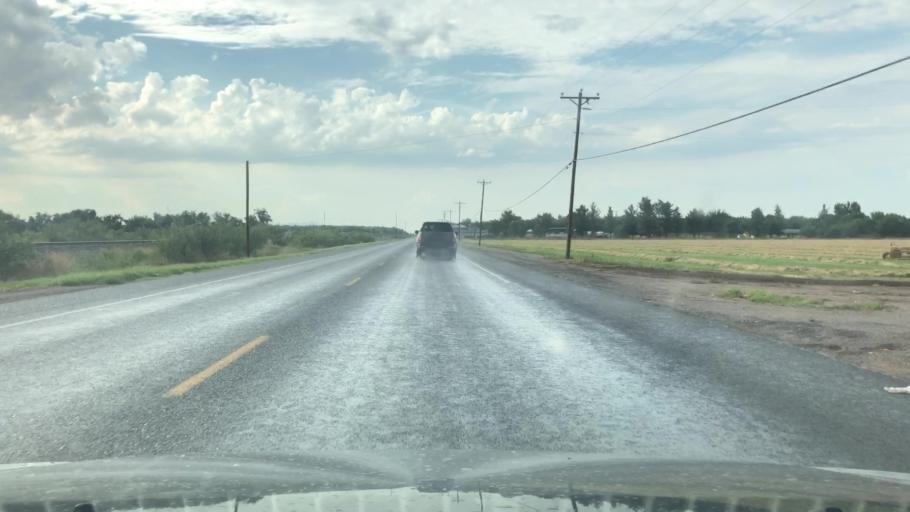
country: US
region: New Mexico
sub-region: Dona Ana County
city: Mesquite
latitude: 32.2061
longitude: -106.7228
